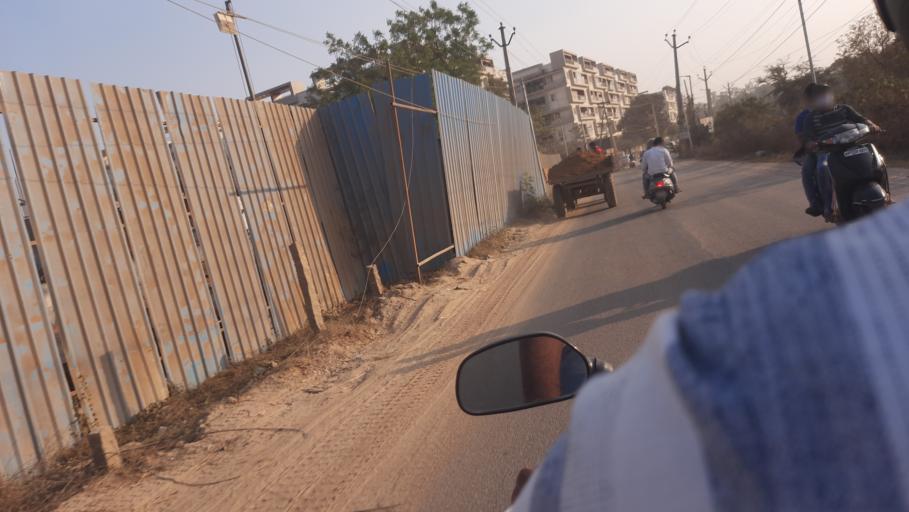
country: IN
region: Telangana
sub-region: Rangareddi
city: Secunderabad
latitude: 17.5213
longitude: 78.5413
